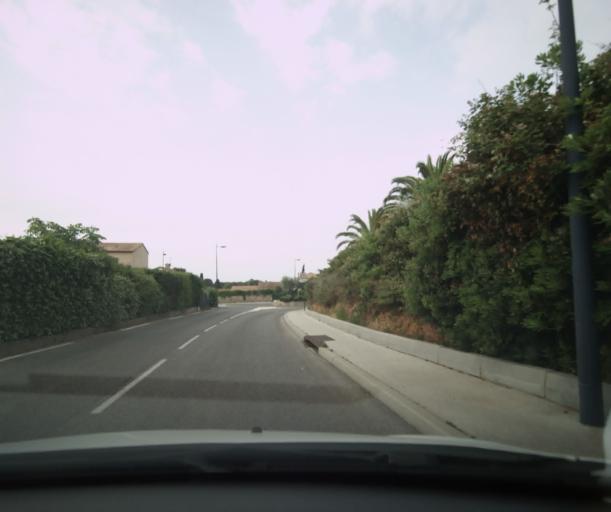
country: FR
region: Provence-Alpes-Cote d'Azur
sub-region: Departement du Var
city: Carqueiranne
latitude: 43.0976
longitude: 6.0799
